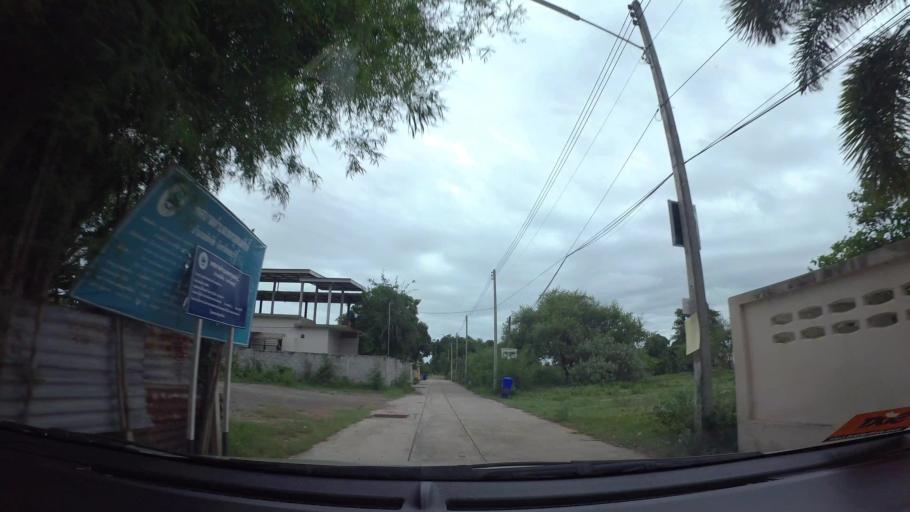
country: TH
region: Chon Buri
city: Sattahip
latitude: 12.6875
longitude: 100.9007
